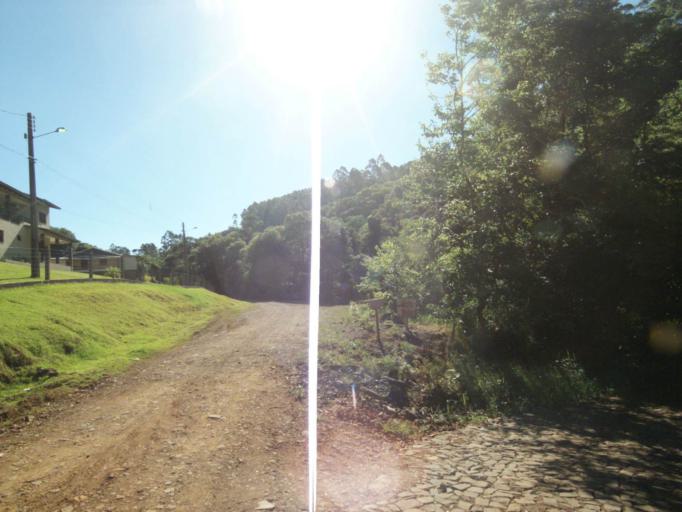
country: BR
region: Parana
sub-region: Ampere
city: Ampere
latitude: -26.1696
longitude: -53.3691
